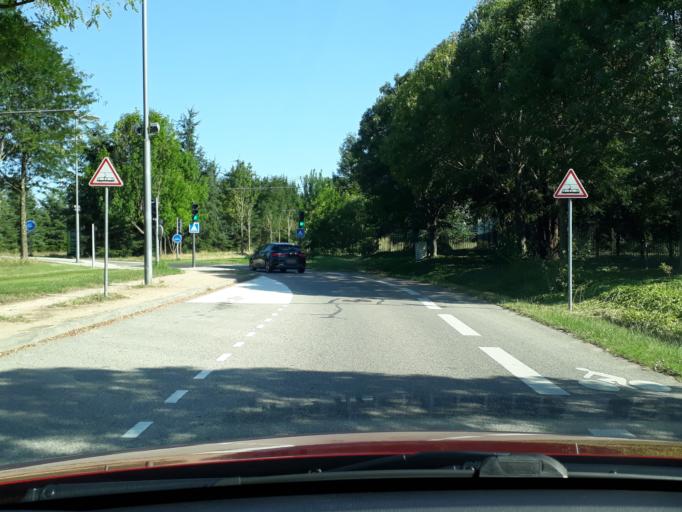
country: FR
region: Rhone-Alpes
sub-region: Departement du Rhone
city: Saint-Priest
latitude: 45.7117
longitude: 4.9351
